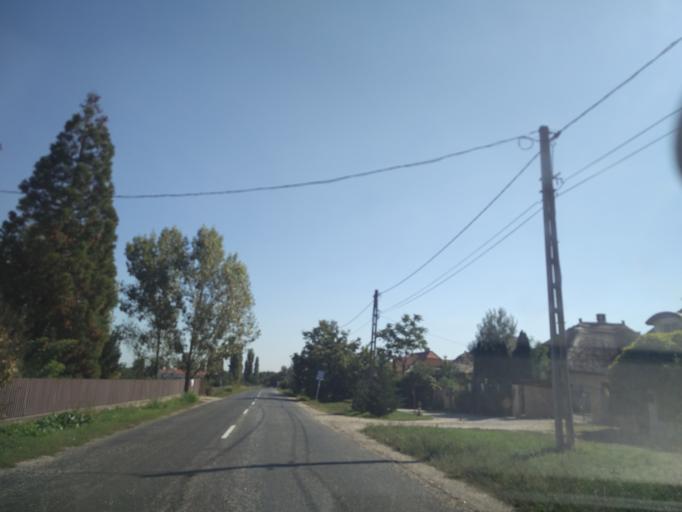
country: HU
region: Fejer
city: Velence
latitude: 47.2483
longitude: 18.6339
